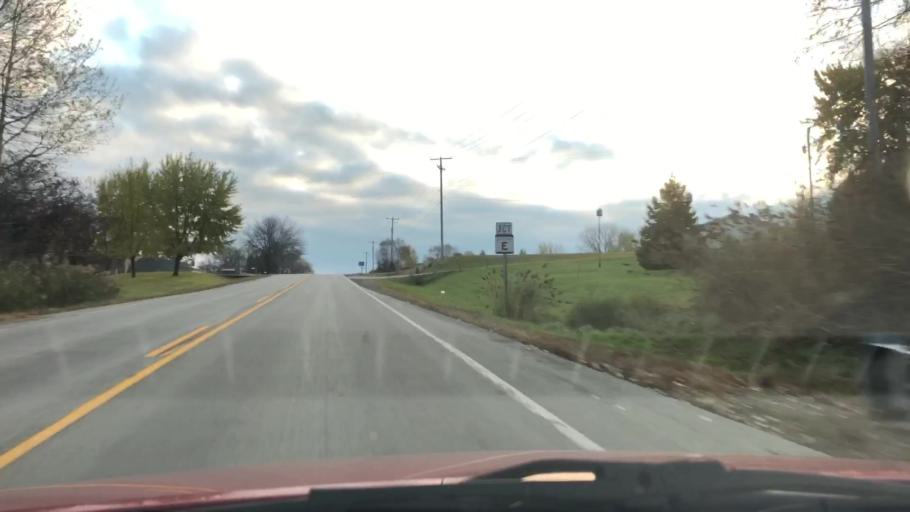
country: US
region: Wisconsin
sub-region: Brown County
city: Oneida
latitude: 44.4443
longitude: -88.2315
